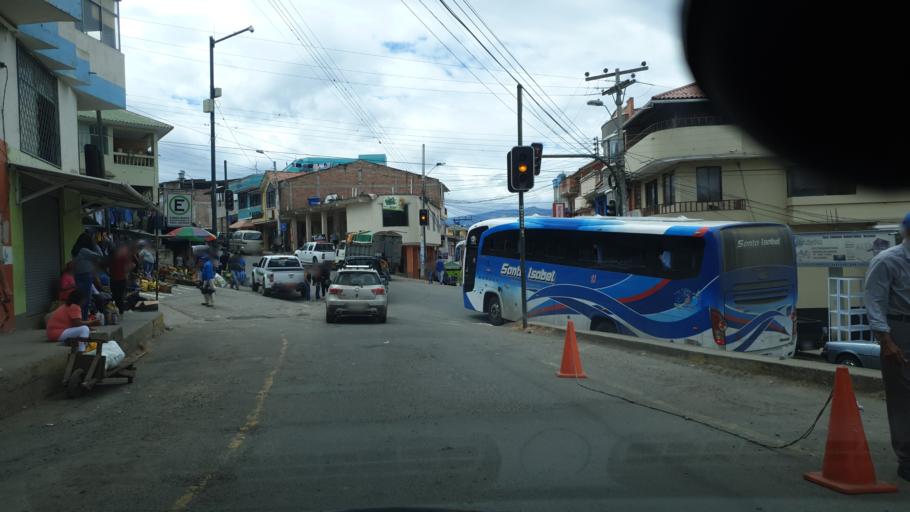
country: EC
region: Azuay
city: Cuenca
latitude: -3.2760
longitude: -79.3143
